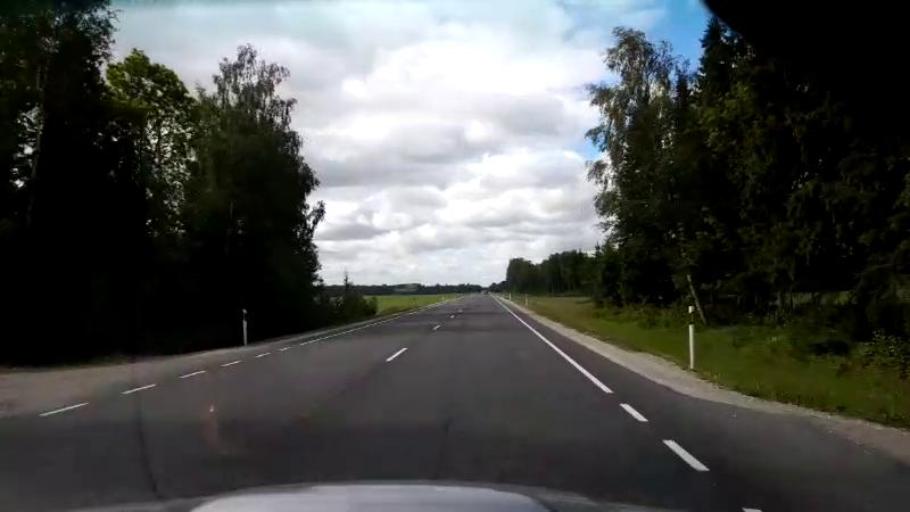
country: EE
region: Raplamaa
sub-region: Maerjamaa vald
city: Marjamaa
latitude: 58.8531
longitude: 24.4316
